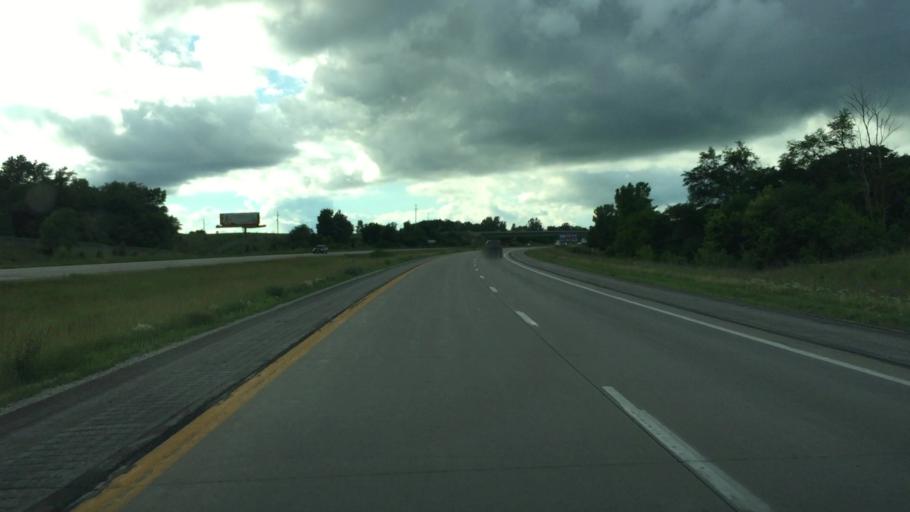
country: US
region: Iowa
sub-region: Polk County
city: Altoona
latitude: 41.6285
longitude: -93.4995
